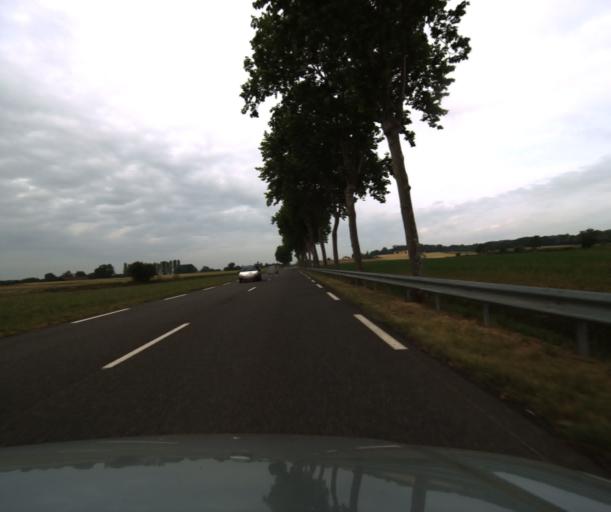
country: FR
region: Midi-Pyrenees
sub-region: Departement du Gers
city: Mielan
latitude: 43.4241
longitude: 0.2798
